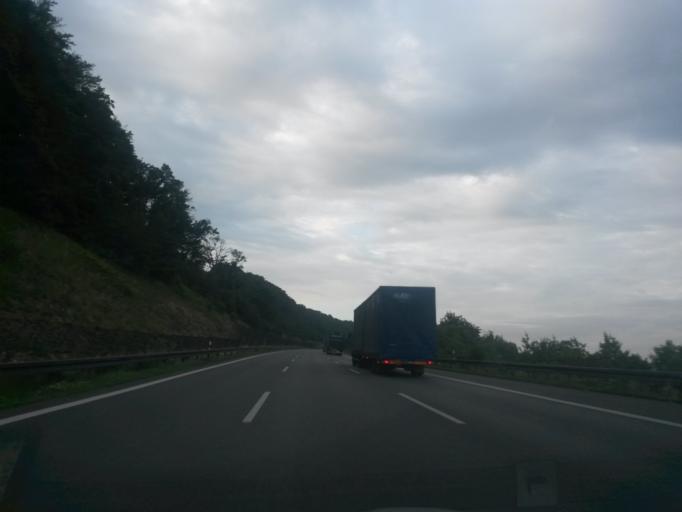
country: DE
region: Bavaria
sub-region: Regierungsbezirk Mittelfranken
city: Greding
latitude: 48.9816
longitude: 11.3925
